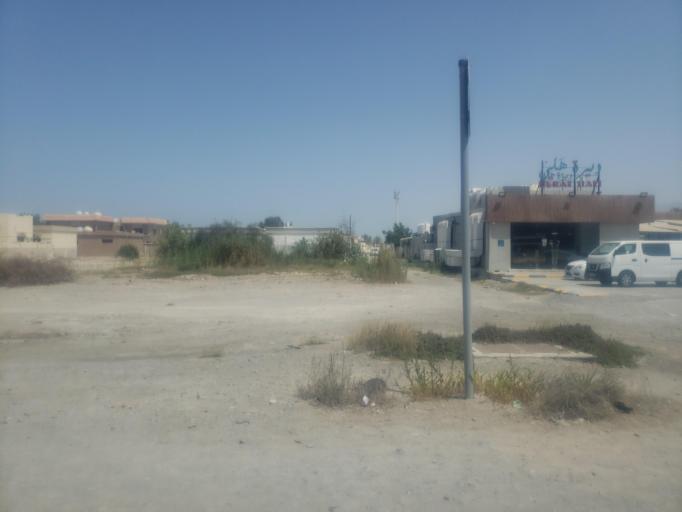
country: AE
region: Ra's al Khaymah
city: Ras al-Khaimah
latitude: 25.8035
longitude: 55.9682
